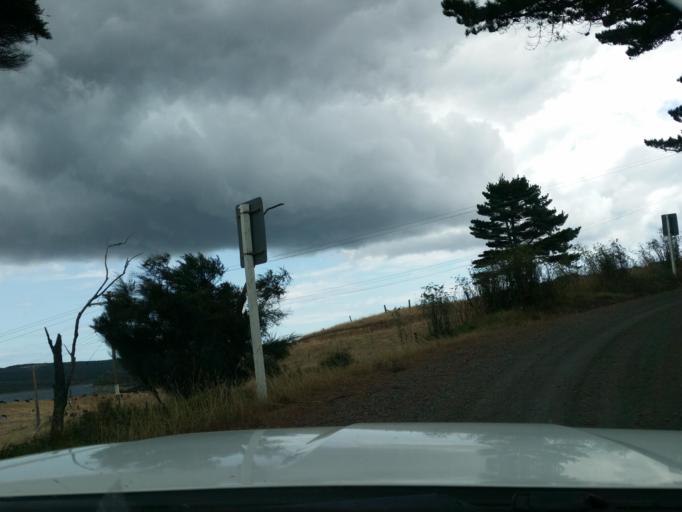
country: NZ
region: Auckland
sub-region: Auckland
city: Wellsford
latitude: -36.3225
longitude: 174.1358
